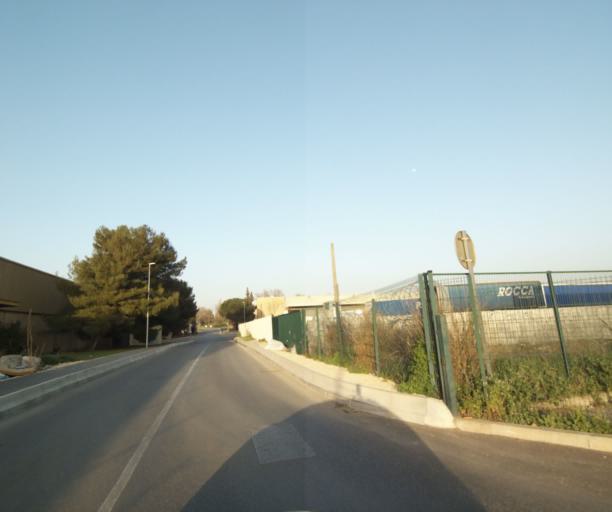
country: FR
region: Provence-Alpes-Cote d'Azur
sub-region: Departement des Bouches-du-Rhone
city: Saint-Victoret
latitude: 43.4187
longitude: 5.2648
